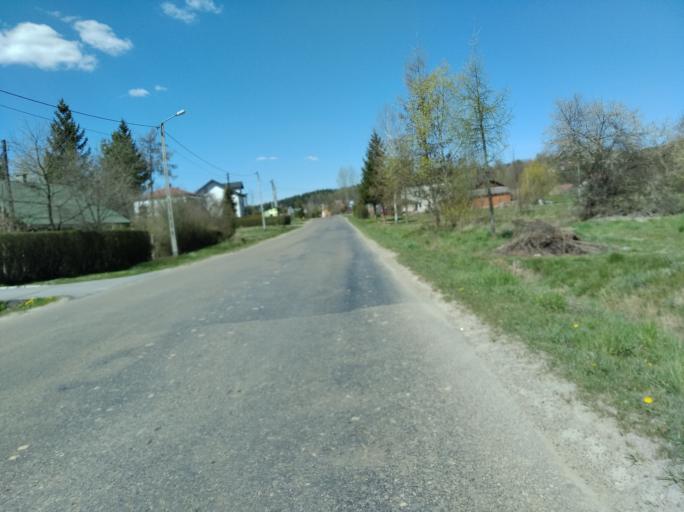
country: PL
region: Subcarpathian Voivodeship
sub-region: Powiat brzozowski
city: Dydnia
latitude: 49.6939
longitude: 22.1518
